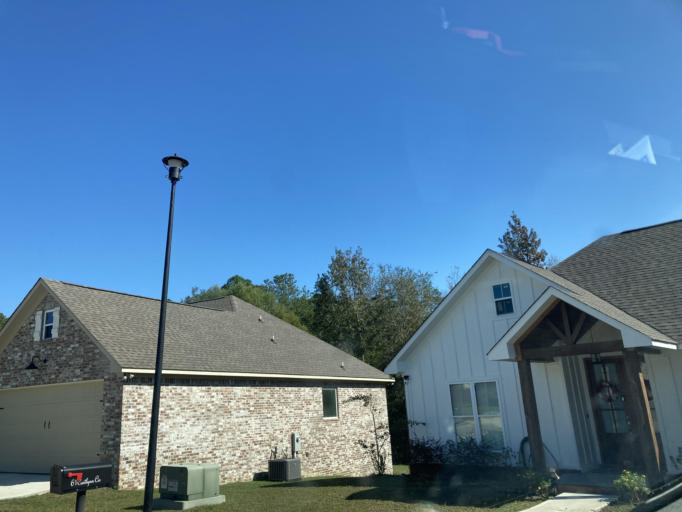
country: US
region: Mississippi
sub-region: Lamar County
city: West Hattiesburg
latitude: 31.3134
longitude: -89.4834
